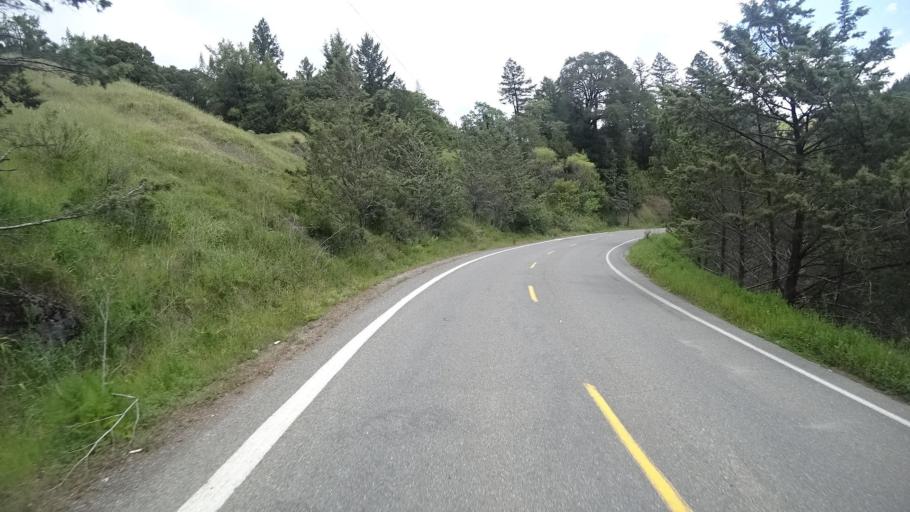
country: US
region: California
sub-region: Humboldt County
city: Redway
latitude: 40.1262
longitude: -123.8709
